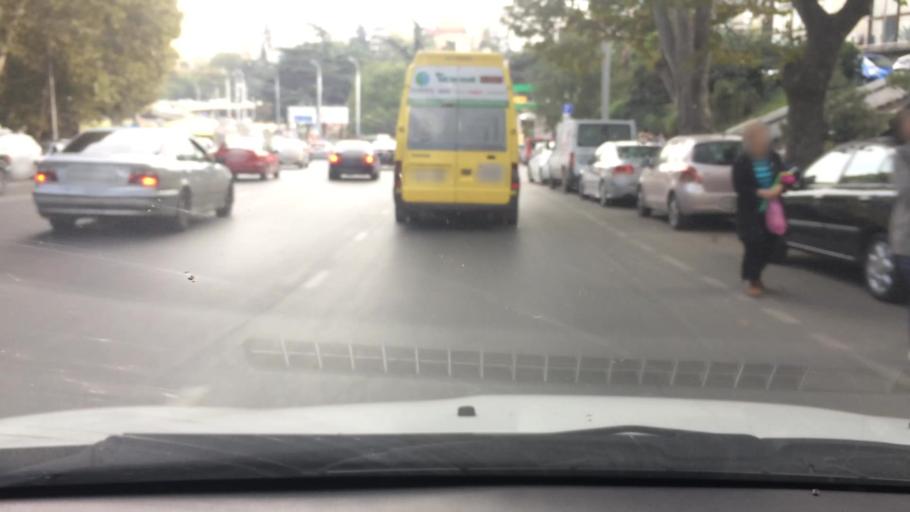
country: GE
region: T'bilisi
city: Tbilisi
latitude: 41.7149
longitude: 44.7793
